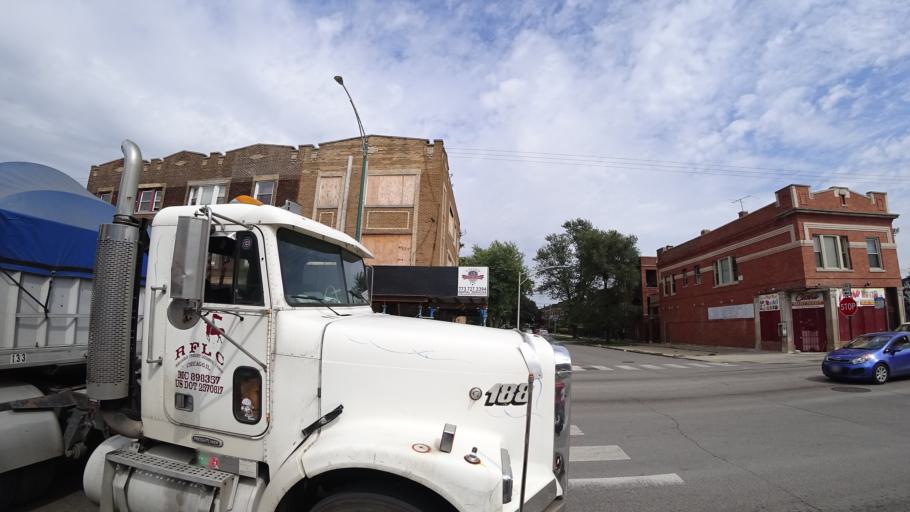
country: US
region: Illinois
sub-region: Cook County
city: Cicero
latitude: 41.8752
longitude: -87.7451
